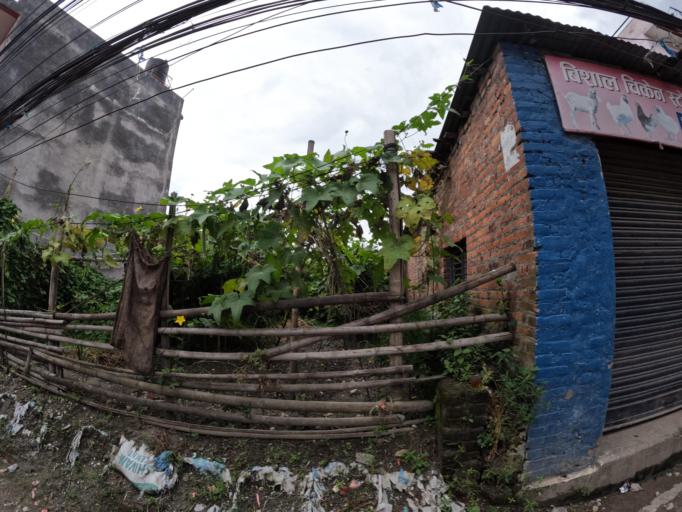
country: NP
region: Central Region
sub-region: Bagmati Zone
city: Kathmandu
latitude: 27.7449
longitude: 85.3198
